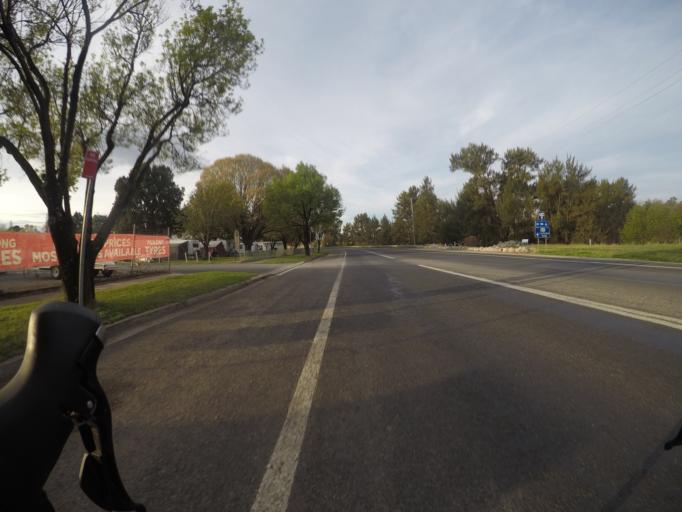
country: AU
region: New South Wales
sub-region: Cabonne
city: Molong
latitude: -33.0915
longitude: 148.8714
